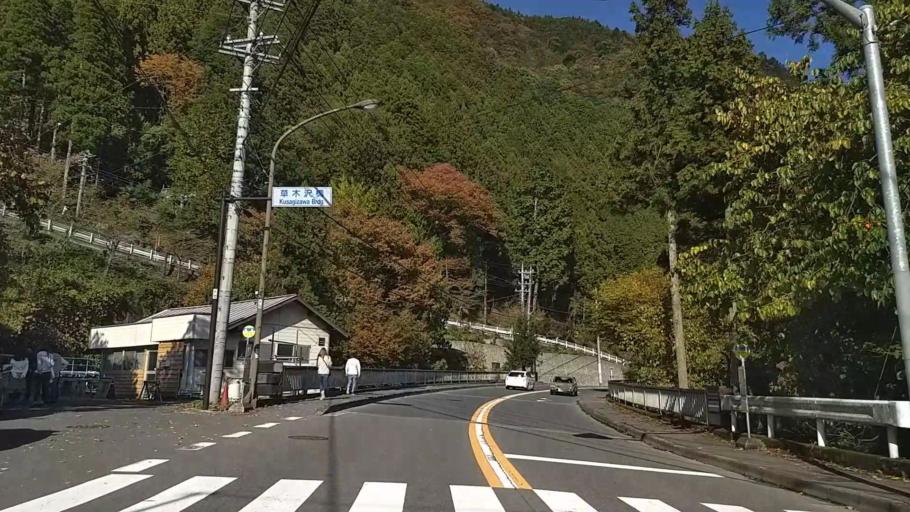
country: JP
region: Tokyo
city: Ome
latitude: 35.8116
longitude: 139.1155
